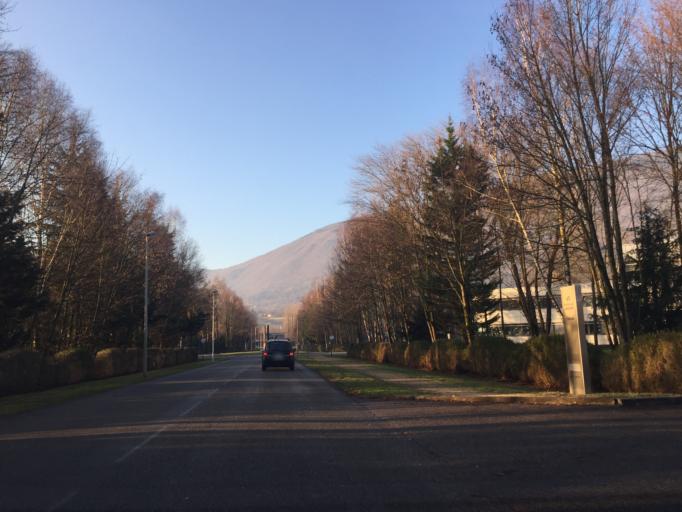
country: FR
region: Rhone-Alpes
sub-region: Departement de la Savoie
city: Le Bourget-du-Lac
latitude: 45.6470
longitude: 5.8726
